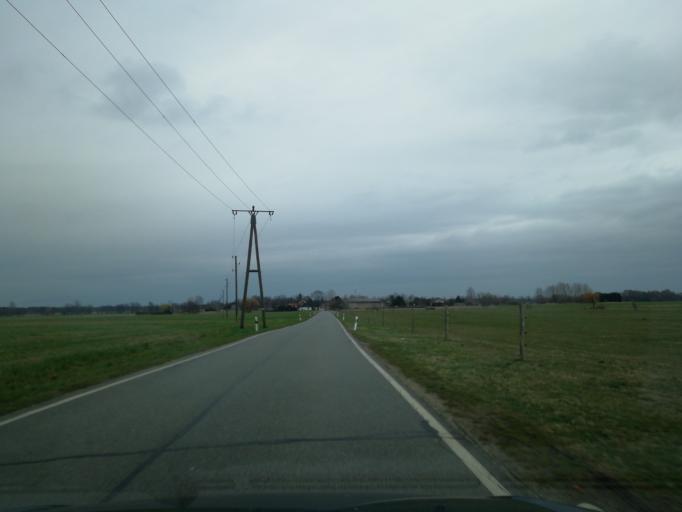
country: DE
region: Brandenburg
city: Vetschau
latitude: 51.7287
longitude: 14.0336
